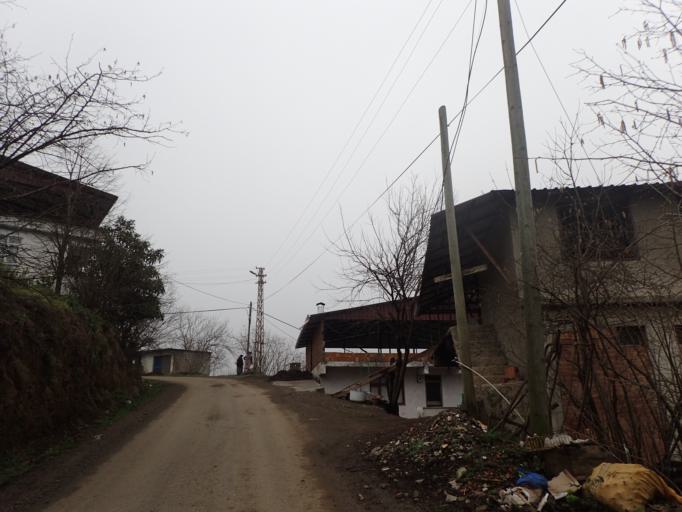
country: TR
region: Ordu
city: Camas
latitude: 40.9219
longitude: 37.5564
